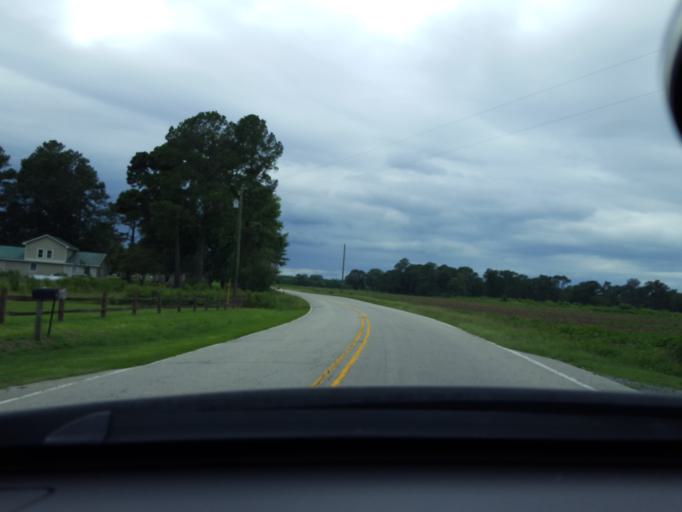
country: US
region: North Carolina
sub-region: Duplin County
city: Rose Hill
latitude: 34.8269
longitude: -78.1541
